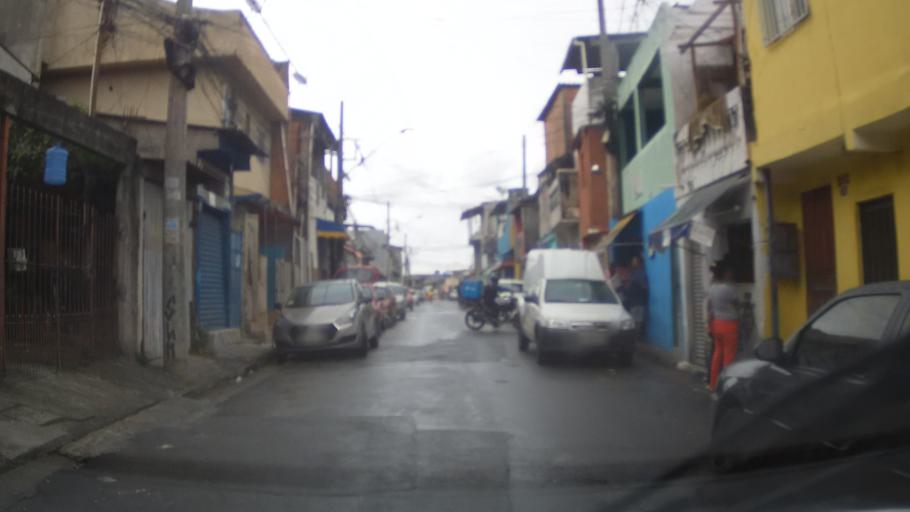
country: BR
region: Sao Paulo
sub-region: Guarulhos
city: Guarulhos
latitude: -23.4700
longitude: -46.5579
